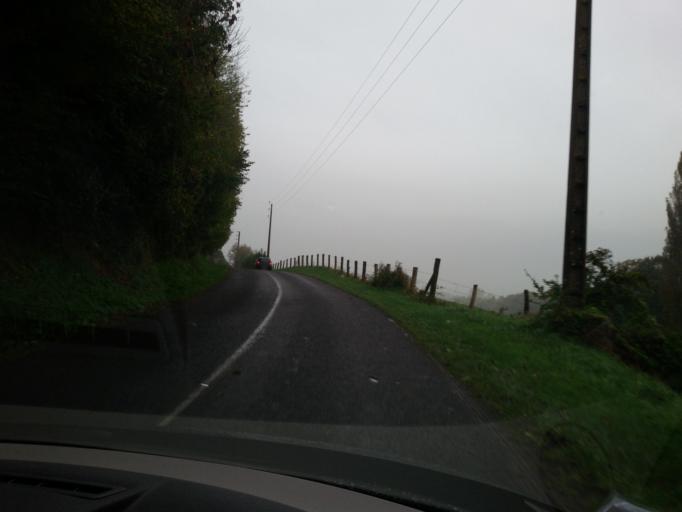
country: FR
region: Lower Normandy
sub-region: Departement du Calvados
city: Ablon
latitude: 49.4254
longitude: 0.3327
